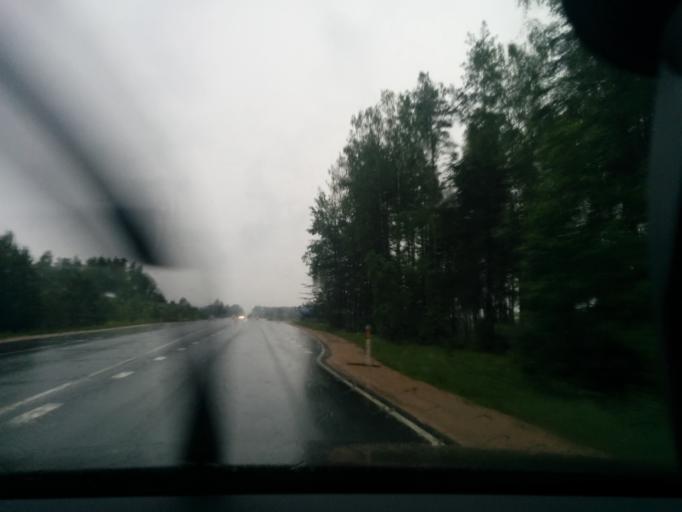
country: LV
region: Ikskile
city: Ikskile
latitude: 56.8861
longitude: 24.4929
